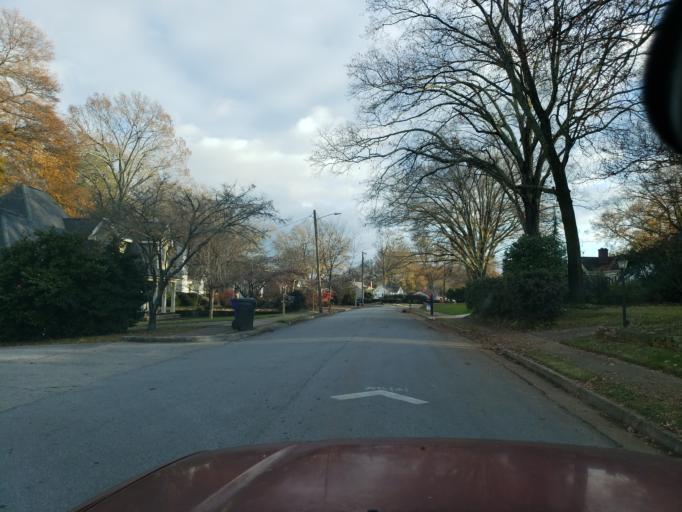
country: US
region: South Carolina
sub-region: Greenville County
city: Greenville
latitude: 34.8329
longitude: -82.3533
